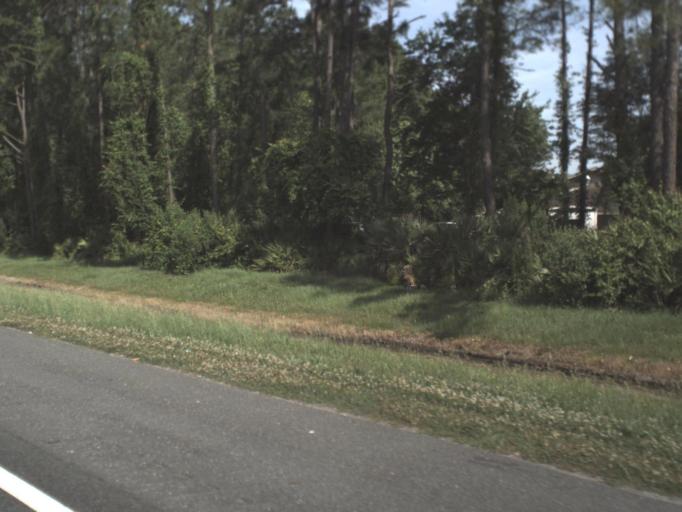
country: US
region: Florida
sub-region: Saint Johns County
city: Ponte Vedra Beach
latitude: 30.2519
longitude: -81.4567
